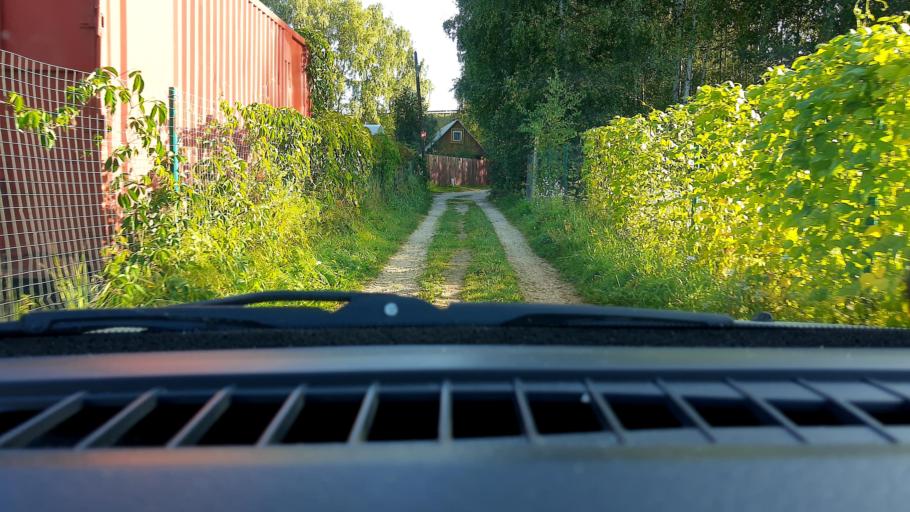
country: RU
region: Nizjnij Novgorod
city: Sitniki
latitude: 56.4684
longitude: 44.0351
